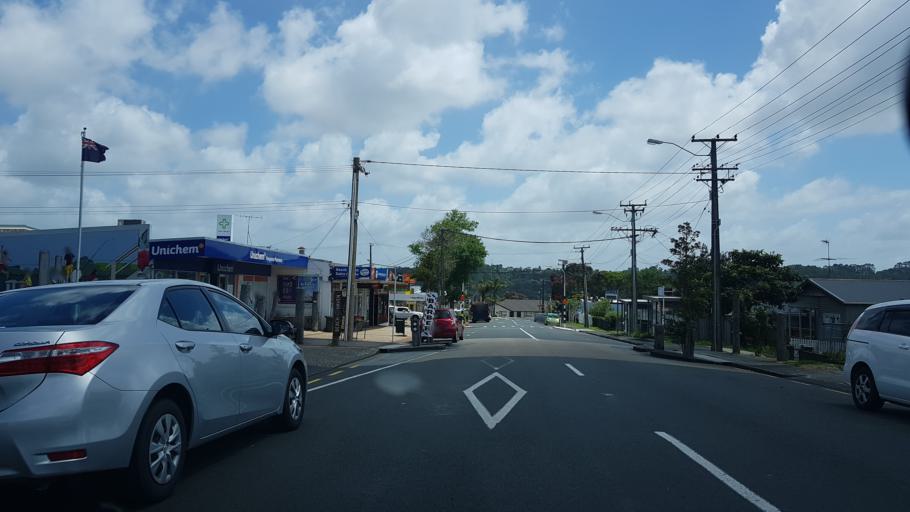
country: NZ
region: Auckland
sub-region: Auckland
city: North Shore
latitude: -36.7930
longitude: 174.6879
